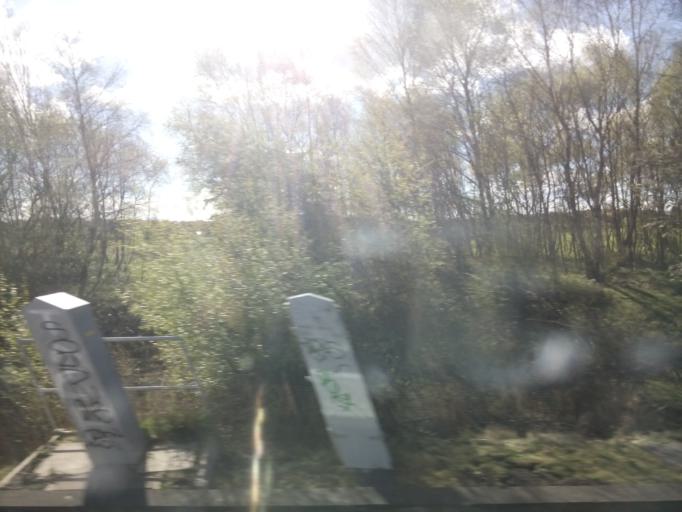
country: GB
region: England
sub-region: Northumberland
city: Seghill
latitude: 55.0389
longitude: -1.5863
